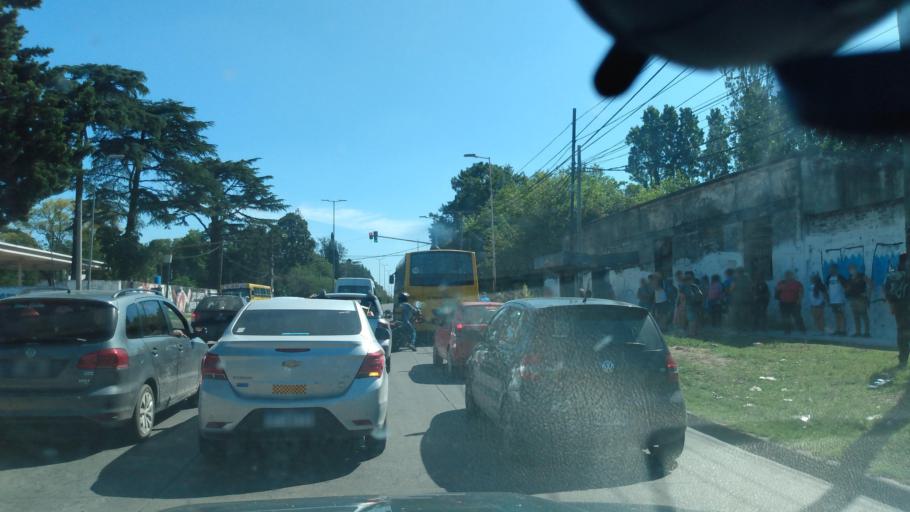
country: AR
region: Buenos Aires
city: Hurlingham
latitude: -34.5569
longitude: -58.7277
